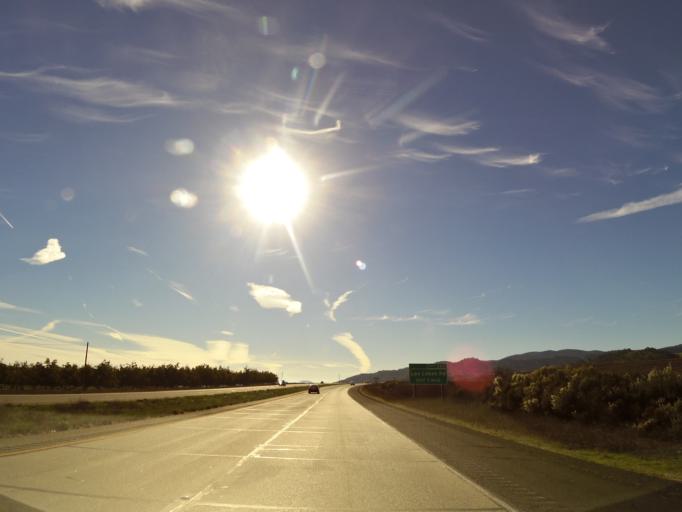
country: US
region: California
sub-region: San Luis Obispo County
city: Lake Nacimiento
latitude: 35.9889
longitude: -120.9052
